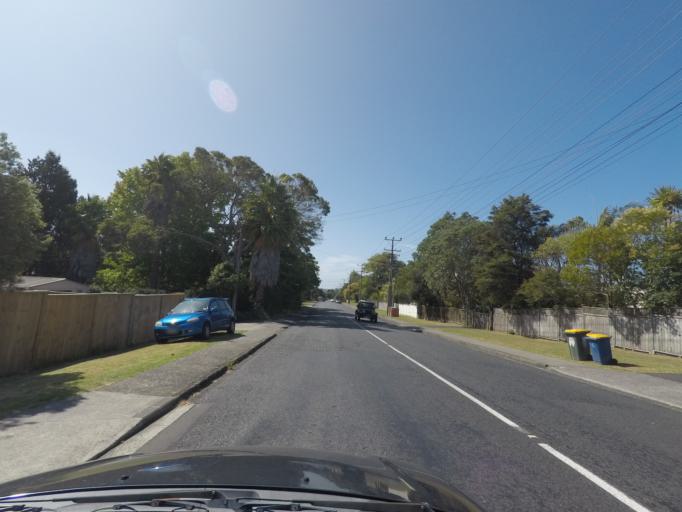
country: NZ
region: Auckland
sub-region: Auckland
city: Titirangi
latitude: -36.9331
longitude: 174.6552
